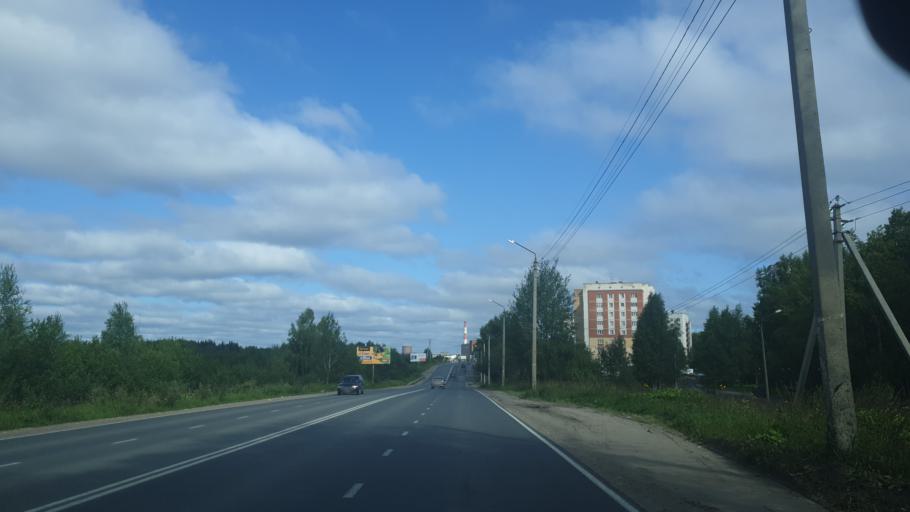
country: RU
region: Komi Republic
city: Ezhva
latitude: 61.7920
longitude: 50.7409
